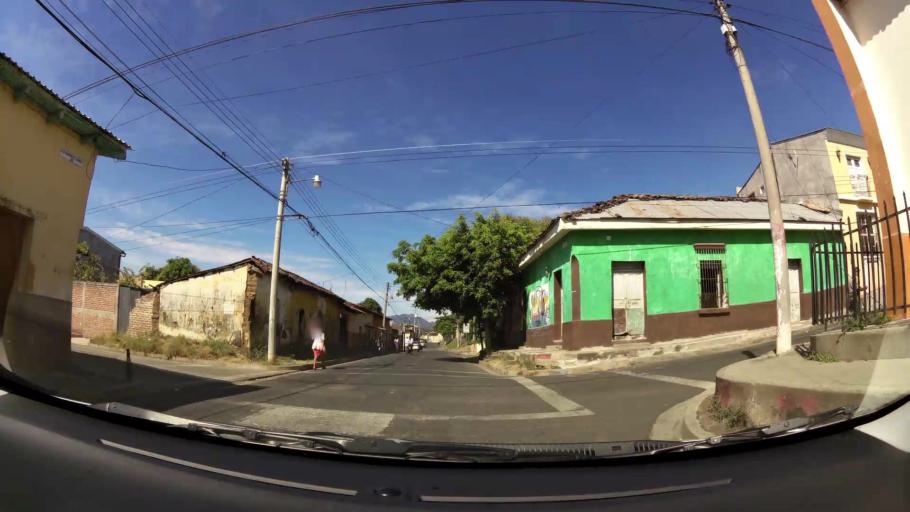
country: SV
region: Santa Ana
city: Chalchuapa
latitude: 13.9848
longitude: -89.6816
